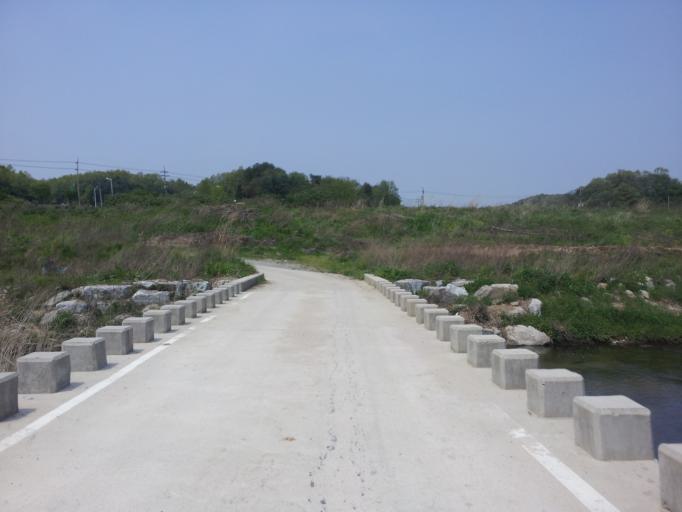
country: KR
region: Daejeon
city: Daejeon
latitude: 36.2657
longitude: 127.2902
